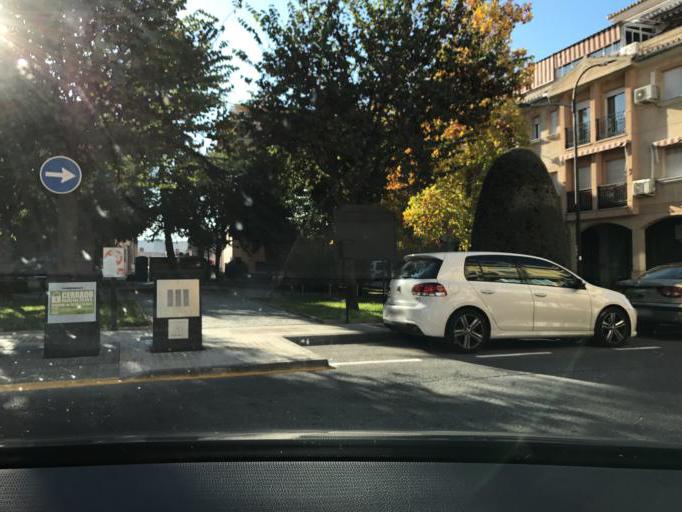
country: ES
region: Andalusia
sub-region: Provincia de Granada
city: Maracena
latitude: 37.2104
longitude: -3.6266
